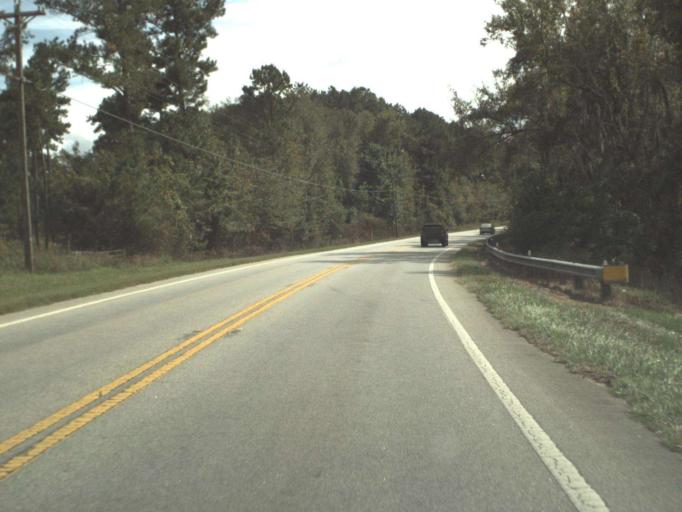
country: US
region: Florida
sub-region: Gadsden County
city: Quincy
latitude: 30.6241
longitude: -84.5959
